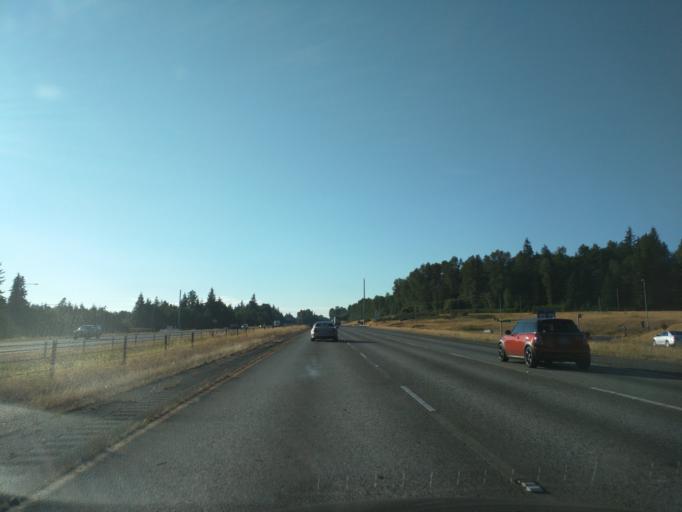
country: US
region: Washington
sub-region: Snohomish County
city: Bryant
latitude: 48.2372
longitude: -122.2394
